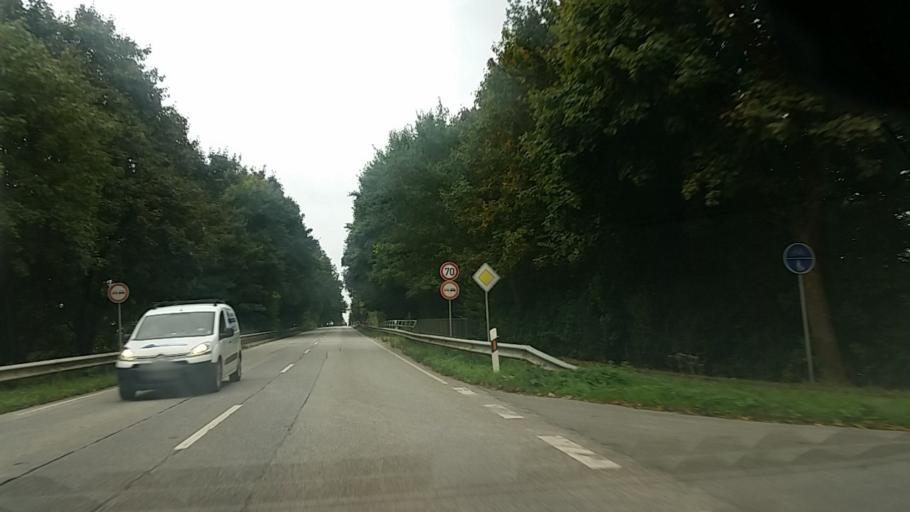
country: DE
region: Schleswig-Holstein
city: Mozen
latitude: 53.9079
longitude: 10.2618
